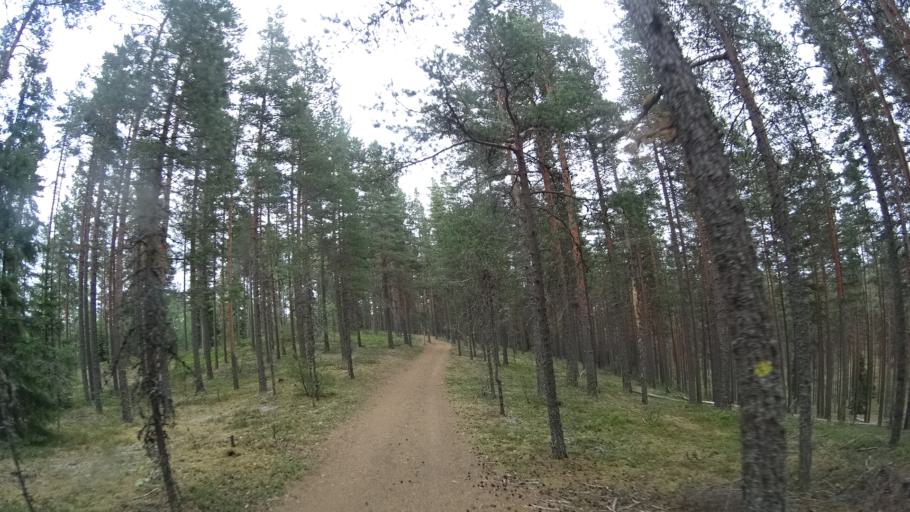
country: FI
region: Satakunta
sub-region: Pohjois-Satakunta
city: Jaemijaervi
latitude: 61.7734
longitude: 22.7315
